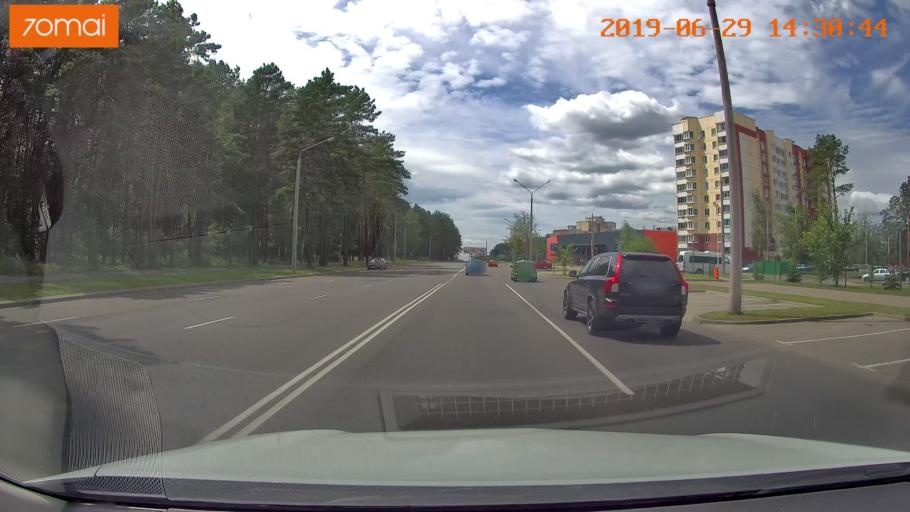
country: BY
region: Minsk
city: Salihorsk
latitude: 52.7814
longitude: 27.5146
